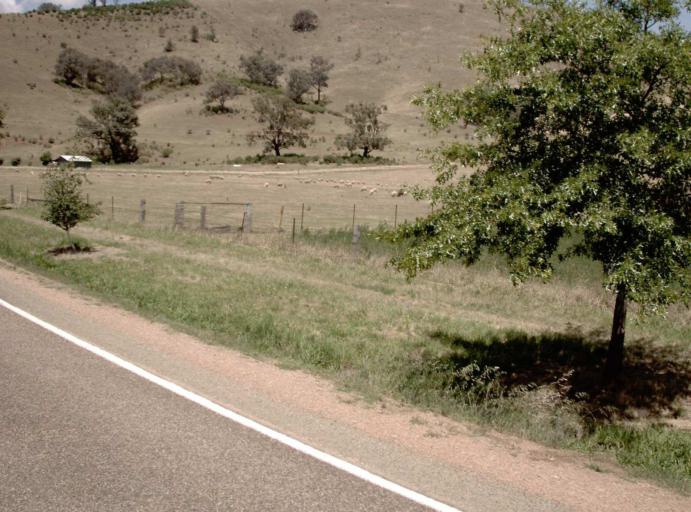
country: AU
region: Victoria
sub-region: East Gippsland
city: Bairnsdale
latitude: -37.2556
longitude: 147.7113
